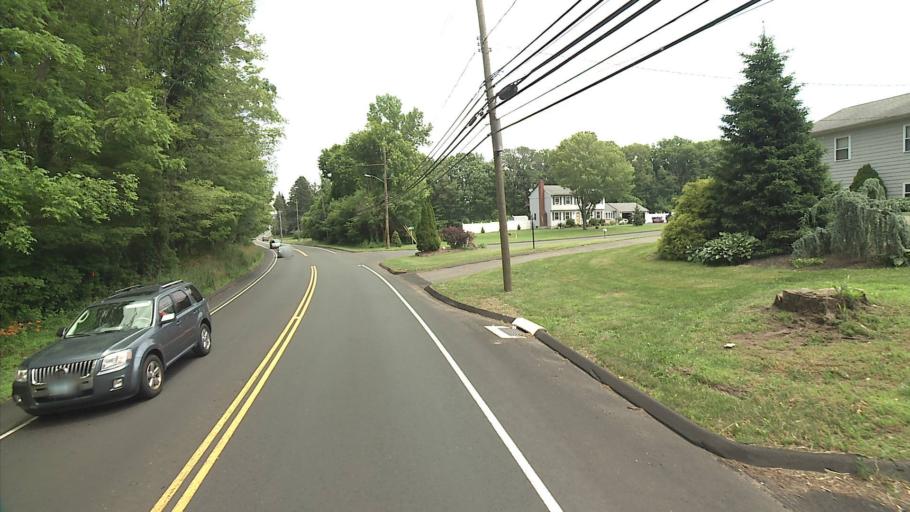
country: US
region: Connecticut
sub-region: New Haven County
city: North Branford
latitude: 41.3721
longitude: -72.7940
